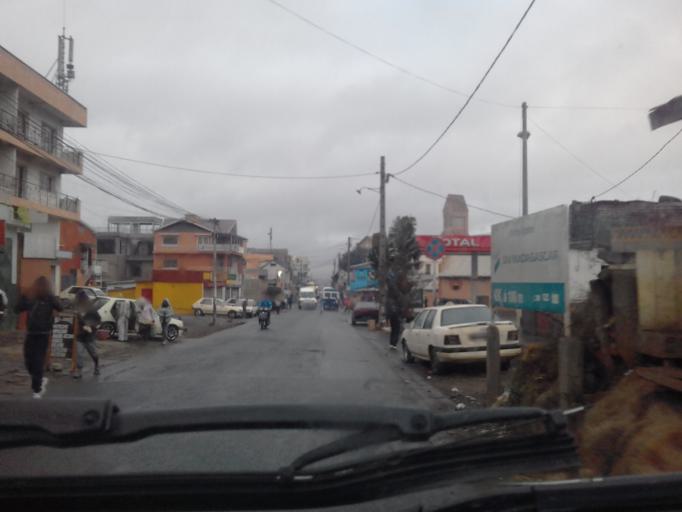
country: MG
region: Analamanga
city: Antananarivo
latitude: -18.8735
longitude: 47.5506
